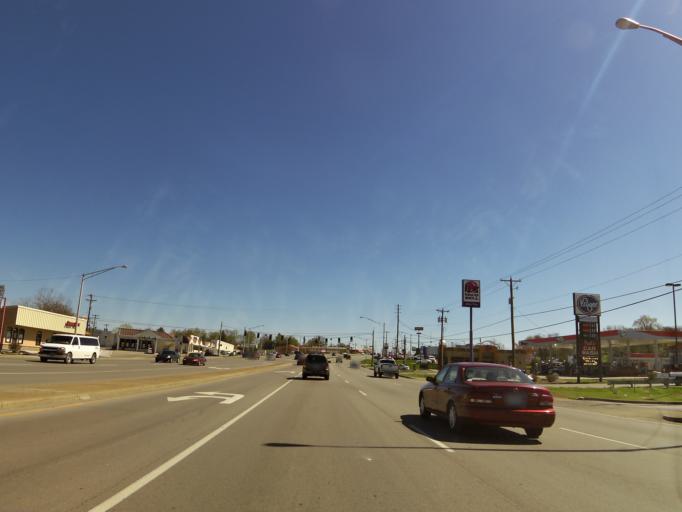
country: US
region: Kentucky
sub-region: Pulaski County
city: Somerset
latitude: 37.0920
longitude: -84.6179
